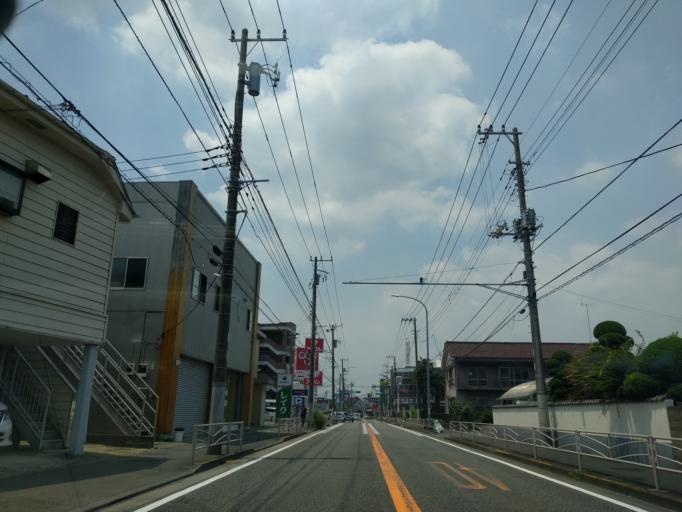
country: JP
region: Kanagawa
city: Minami-rinkan
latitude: 35.4807
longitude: 139.5346
